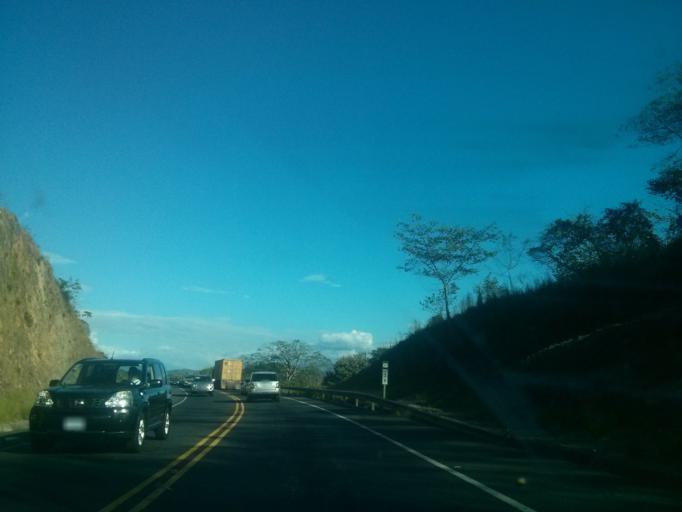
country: CR
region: Alajuela
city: Atenas
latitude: 9.9413
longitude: -84.3894
